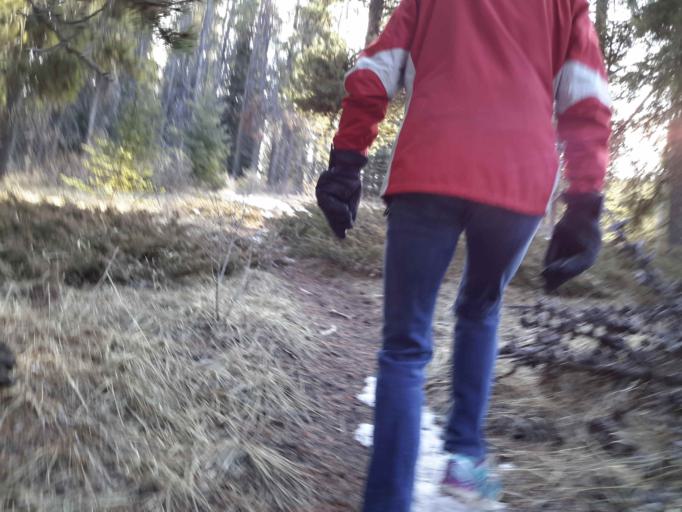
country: CA
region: Alberta
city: Banff
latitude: 51.2010
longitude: -115.5334
